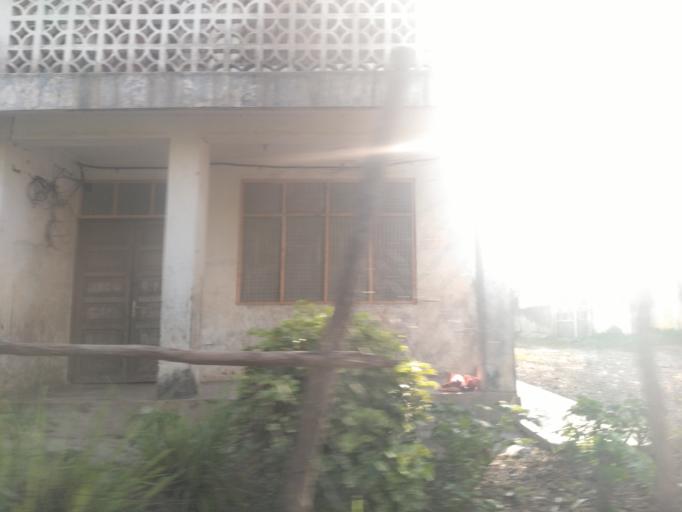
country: TZ
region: Zanzibar Urban/West
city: Zanzibar
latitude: -6.1716
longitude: 39.1960
